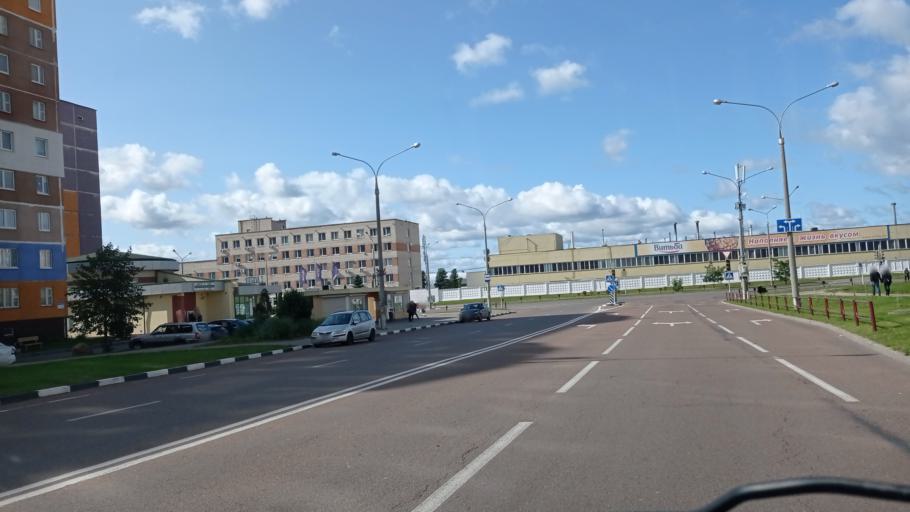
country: BY
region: Vitebsk
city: Vitebsk
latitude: 55.1701
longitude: 30.2586
